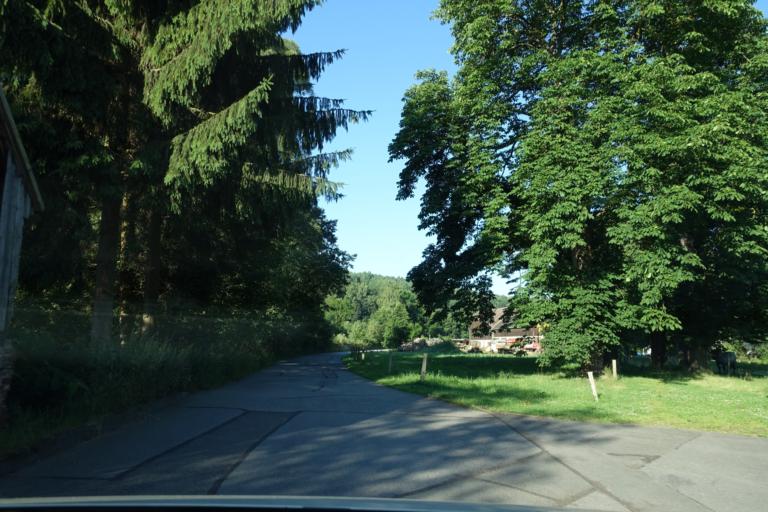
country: DE
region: Saxony
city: Falkenau
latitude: 50.8520
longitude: 13.1028
